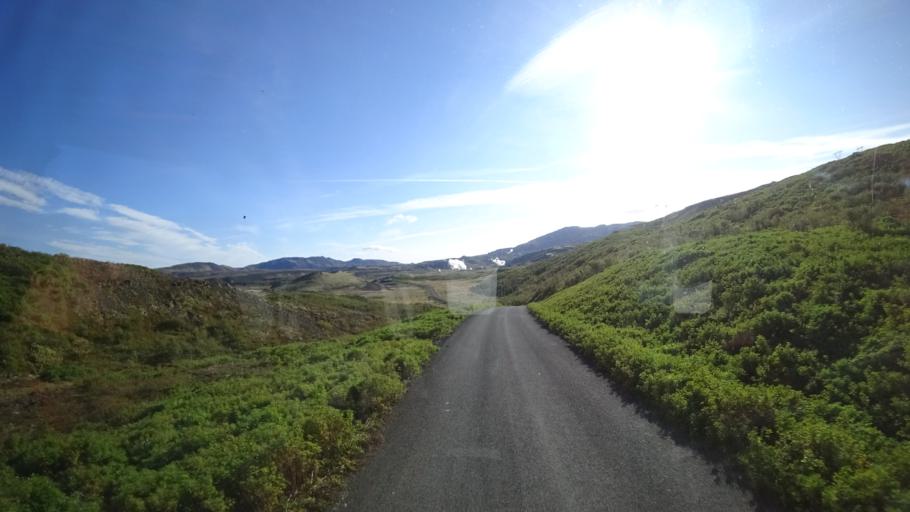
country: IS
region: South
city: Hveragerdi
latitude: 64.1324
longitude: -21.2504
